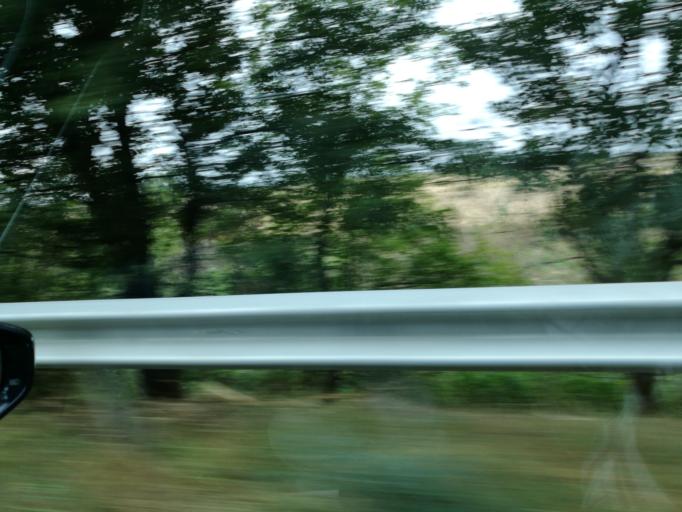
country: RO
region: Braila
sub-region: Municipiul Braila
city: Braila
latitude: 45.2615
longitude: 28.0568
